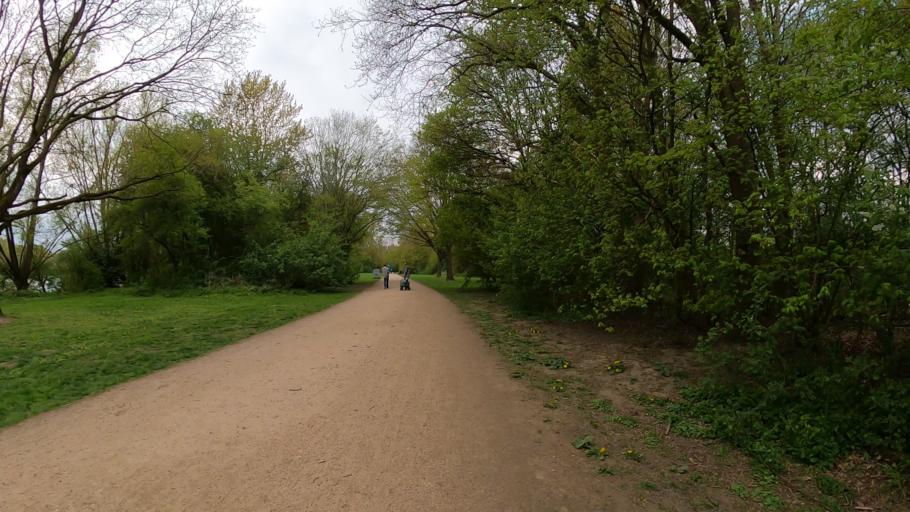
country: DE
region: Hamburg
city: Rothenburgsort
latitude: 53.4843
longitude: 10.0993
